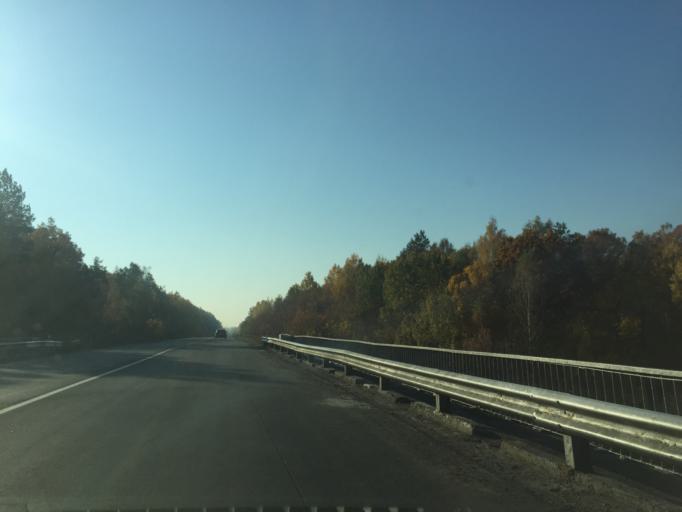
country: BY
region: Gomel
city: Gomel
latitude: 52.4172
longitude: 30.8285
